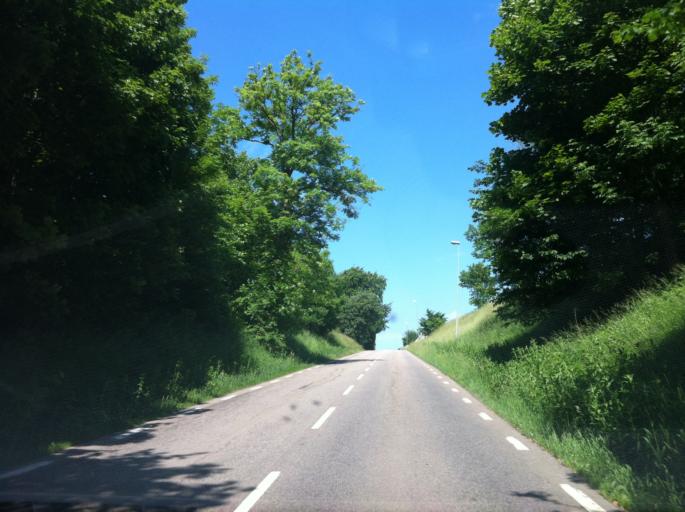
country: SE
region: Skane
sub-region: Helsingborg
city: Glumslov
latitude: 55.9627
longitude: 12.8422
